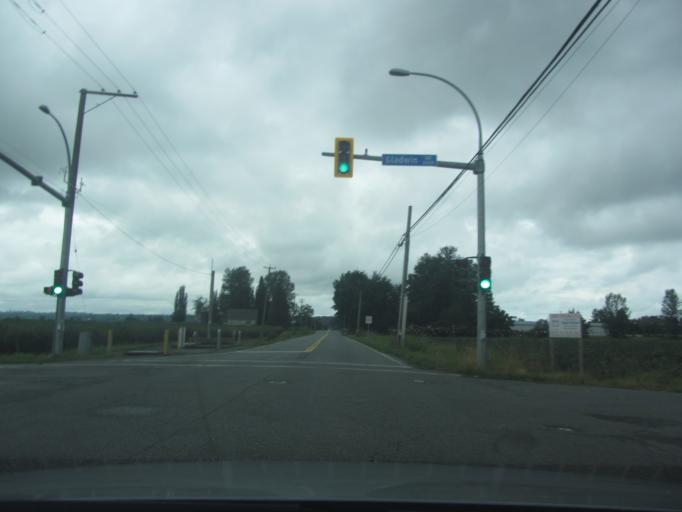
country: CA
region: British Columbia
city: Abbotsford
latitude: 49.1039
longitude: -122.3163
